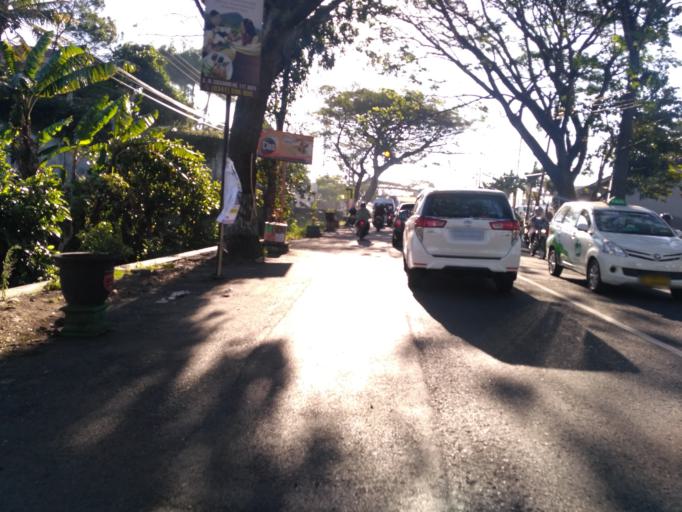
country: ID
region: East Java
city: Batu
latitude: -7.8967
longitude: 112.5552
